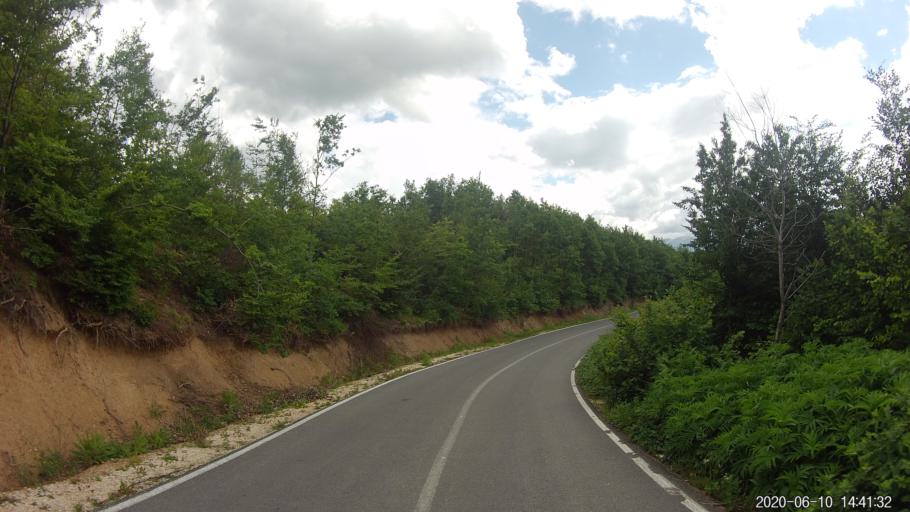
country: XK
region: Prizren
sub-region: Komuna e Therandes
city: Budakovo
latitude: 42.3900
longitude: 20.9447
